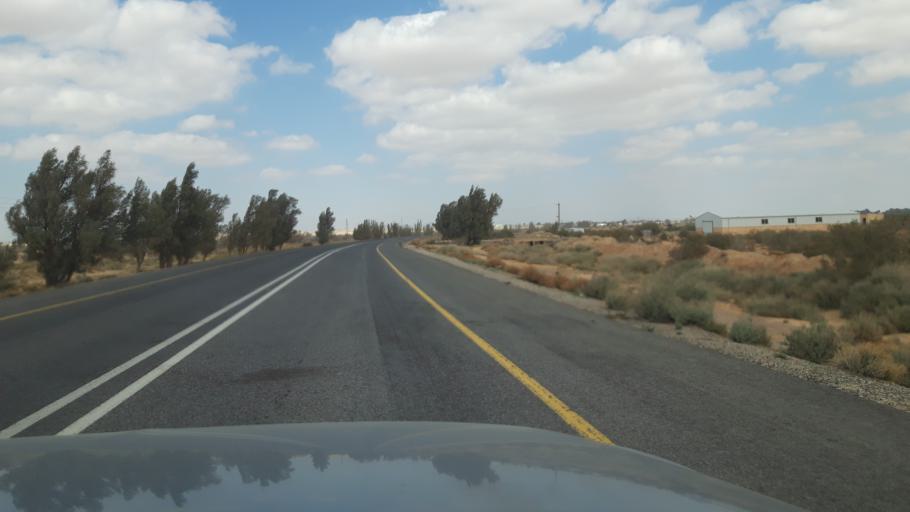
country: JO
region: Amman
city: Al Azraq ash Shamali
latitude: 31.8070
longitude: 36.7967
